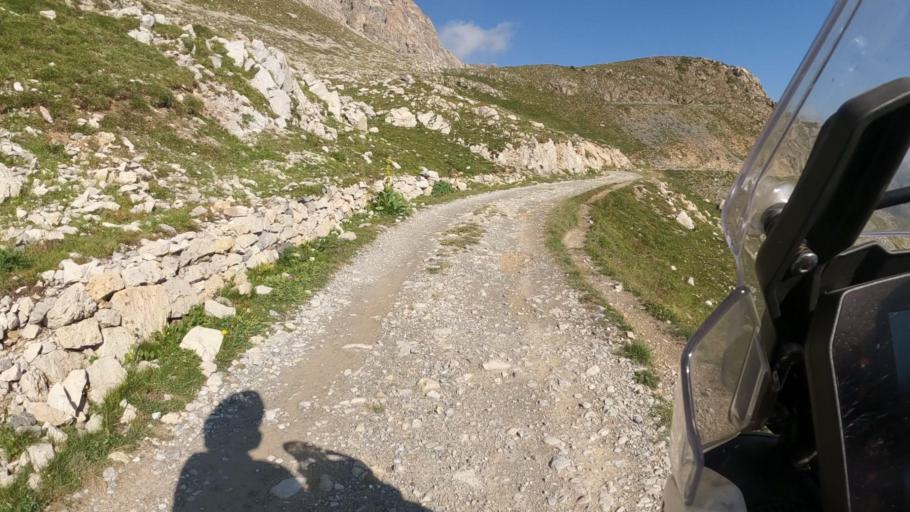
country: IT
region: Piedmont
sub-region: Provincia di Cuneo
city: Pietraporzio
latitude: 44.3884
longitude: 7.0283
